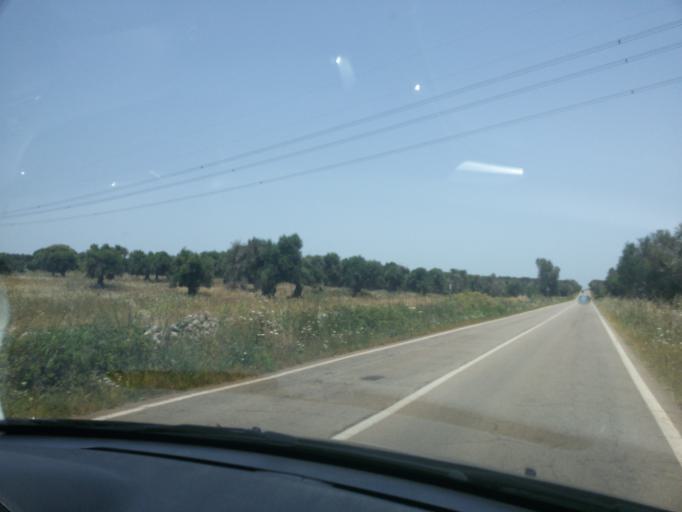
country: IT
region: Apulia
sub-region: Provincia di Lecce
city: Porto Cesareo
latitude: 40.2922
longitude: 17.9146
